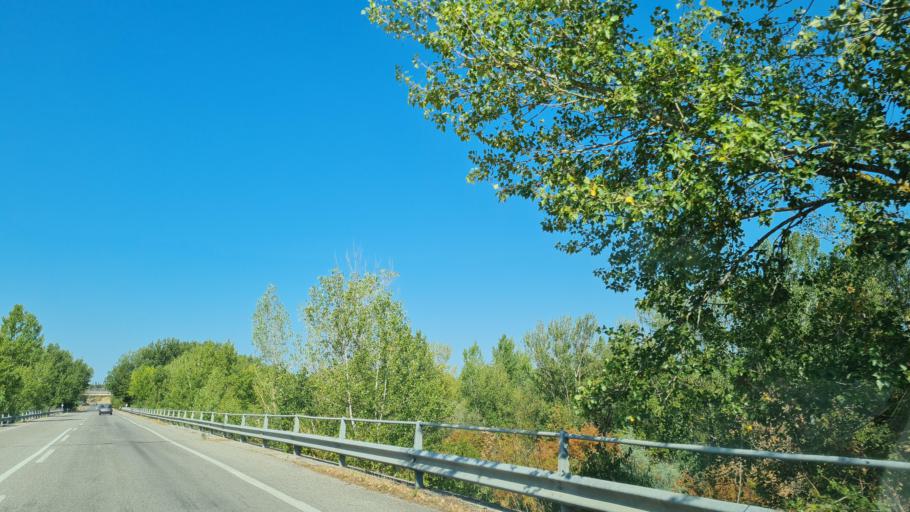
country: IT
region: Tuscany
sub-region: Provincia di Siena
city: Chianciano Terme
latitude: 43.0073
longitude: 11.7411
